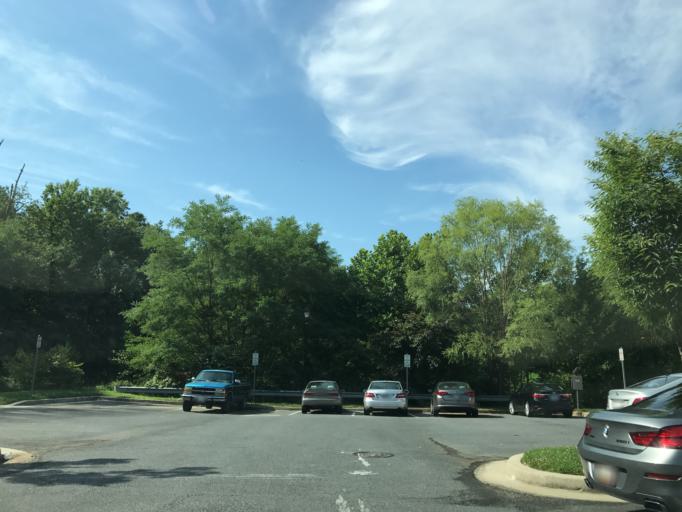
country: US
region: Maryland
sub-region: Baltimore County
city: Rossville
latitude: 39.3470
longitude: -76.4895
